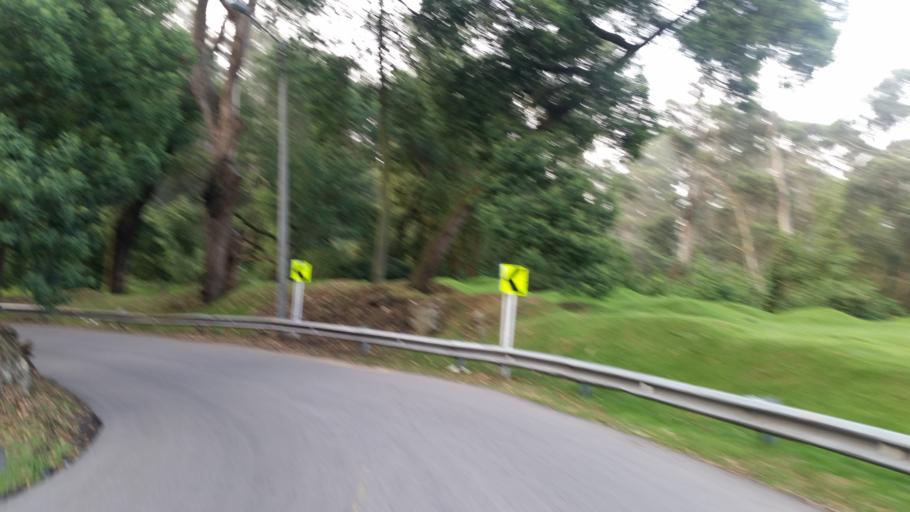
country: CO
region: Bogota D.C.
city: Bogota
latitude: 4.6246
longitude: -74.0594
